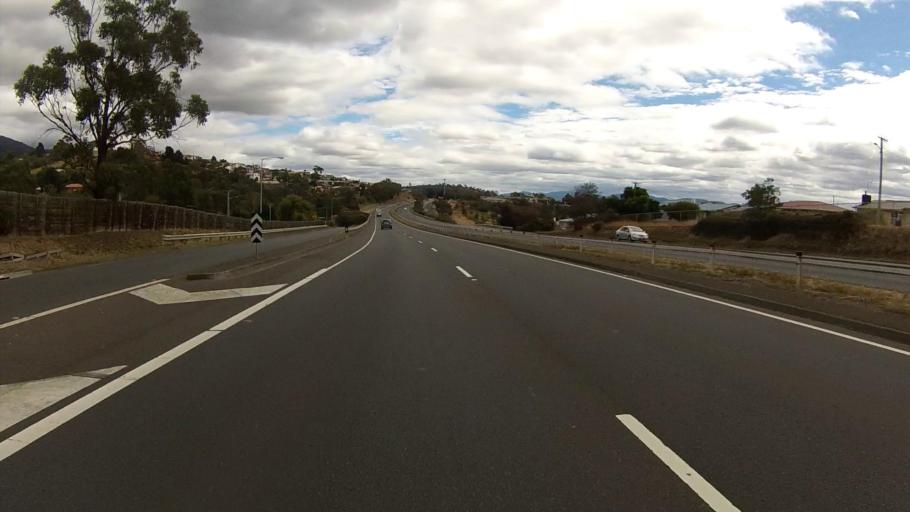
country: AU
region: Tasmania
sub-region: Glenorchy
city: Berriedale
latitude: -42.8022
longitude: 147.2496
